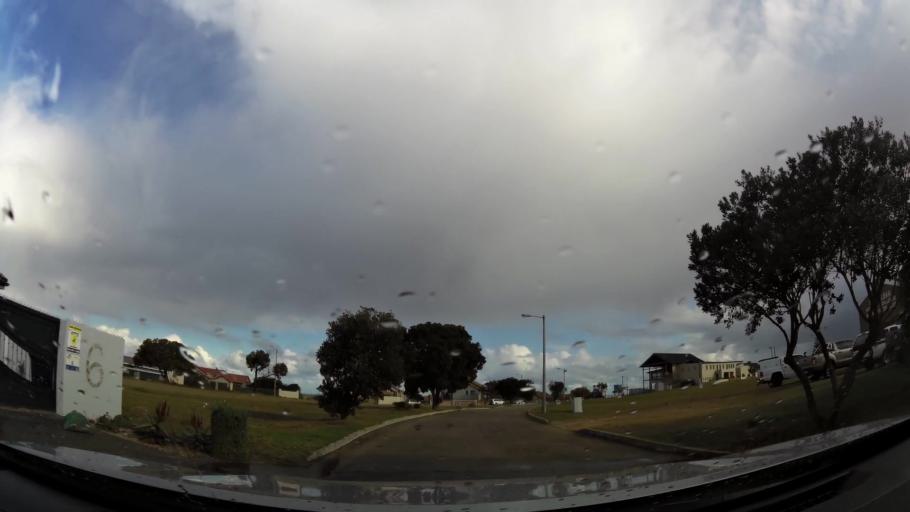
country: ZA
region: Western Cape
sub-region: Eden District Municipality
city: Mossel Bay
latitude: -34.1889
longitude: 22.1228
